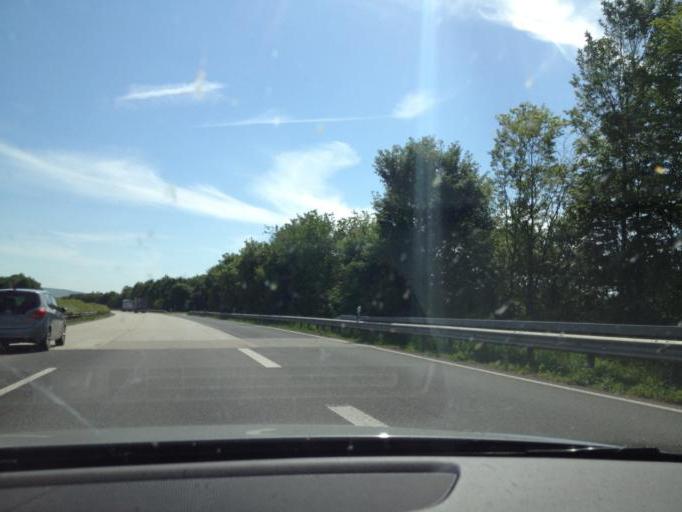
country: DE
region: Rheinland-Pfalz
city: Salmtal
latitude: 49.9230
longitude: 6.8592
